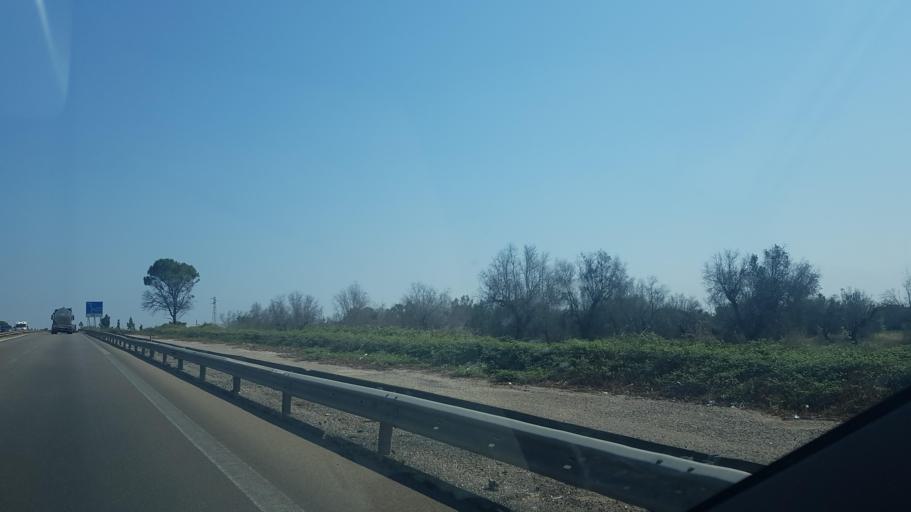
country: IT
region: Apulia
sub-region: Provincia di Lecce
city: Muro Leccese
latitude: 40.1077
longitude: 18.3185
